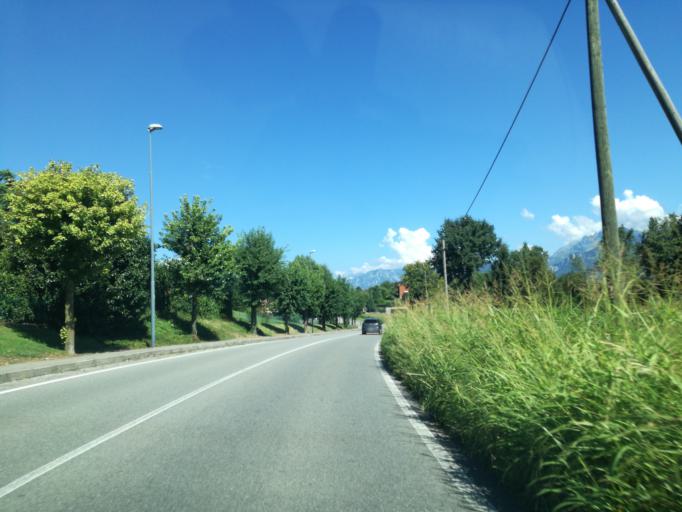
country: IT
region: Lombardy
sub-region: Provincia di Lecco
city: Arlate
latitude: 45.7263
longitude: 9.4424
